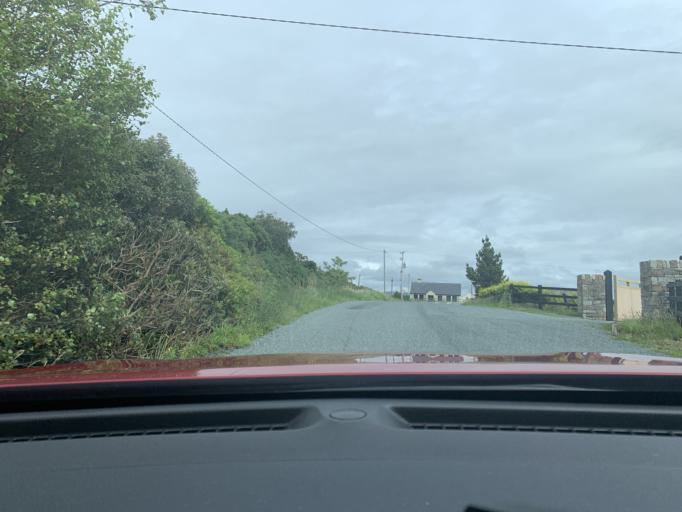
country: IE
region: Ulster
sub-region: County Donegal
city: Dungloe
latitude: 54.9607
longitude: -8.3671
